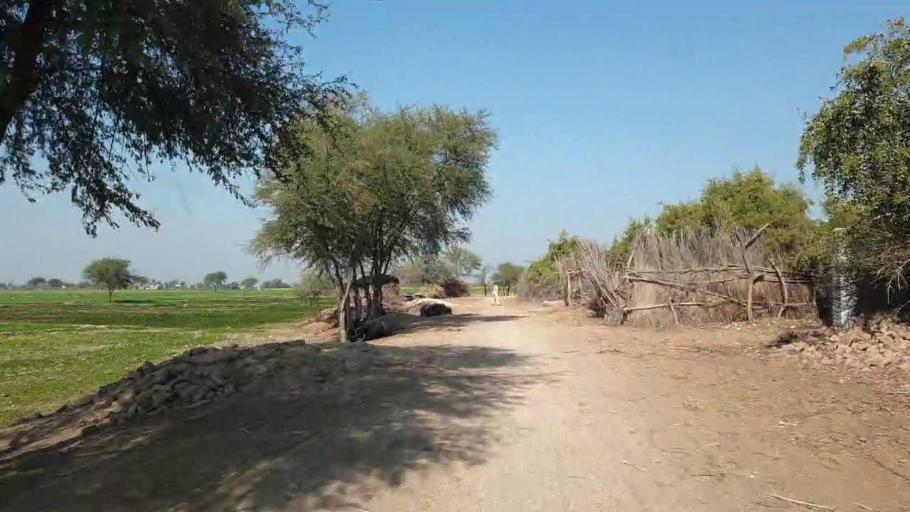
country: PK
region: Sindh
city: Shahdadpur
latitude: 25.9530
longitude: 68.5089
